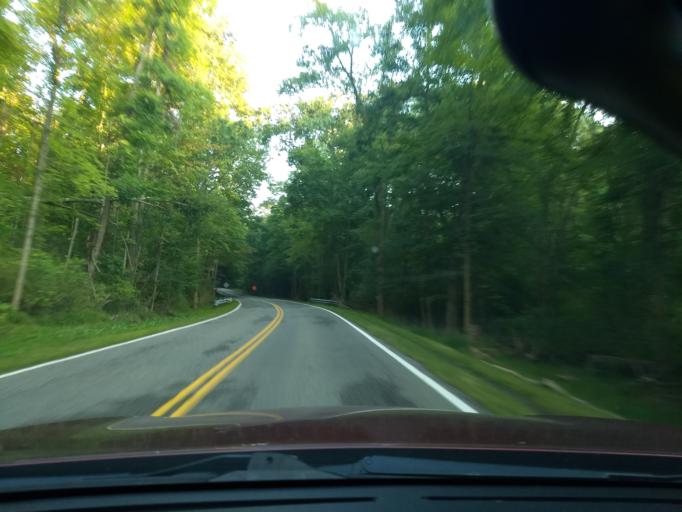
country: US
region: Pennsylvania
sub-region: Allegheny County
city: Bell Acres
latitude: 40.5696
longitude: -80.1568
